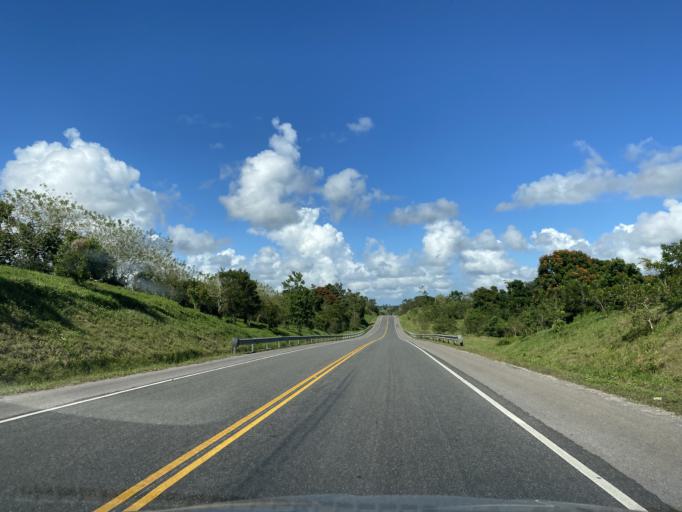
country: DO
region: Monte Plata
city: Majagual
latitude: 19.0145
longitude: -69.8229
